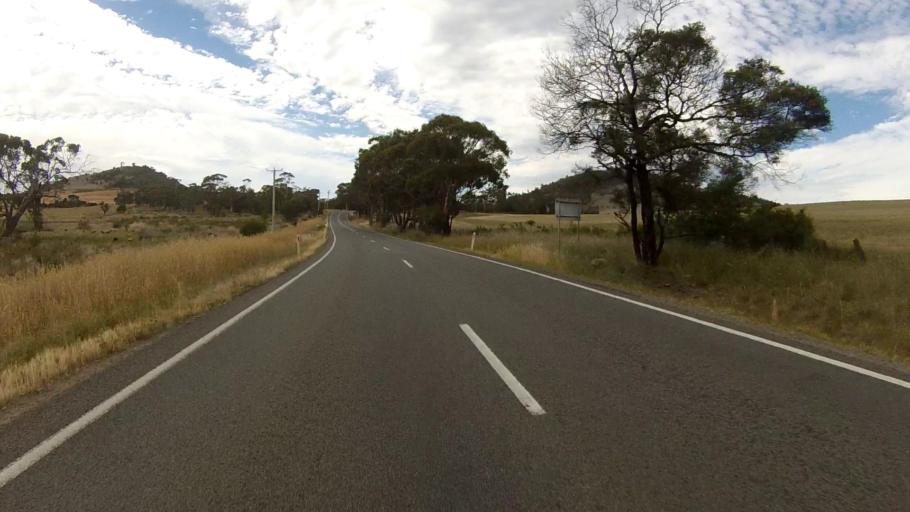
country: AU
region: Tasmania
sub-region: Sorell
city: Sorell
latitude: -42.6998
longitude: 147.4859
